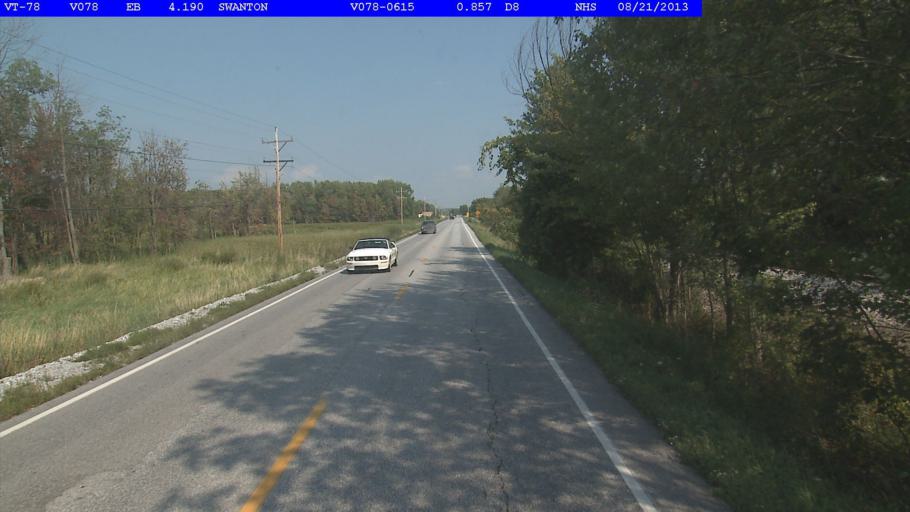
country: US
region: Vermont
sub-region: Franklin County
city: Swanton
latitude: 44.9696
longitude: -73.2038
